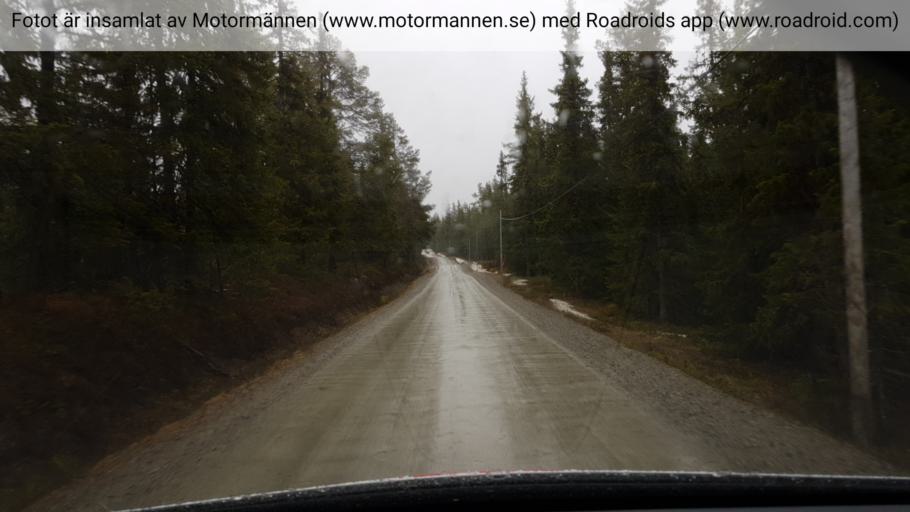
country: SE
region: Jaemtland
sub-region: Are Kommun
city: Are
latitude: 62.6255
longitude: 13.1725
